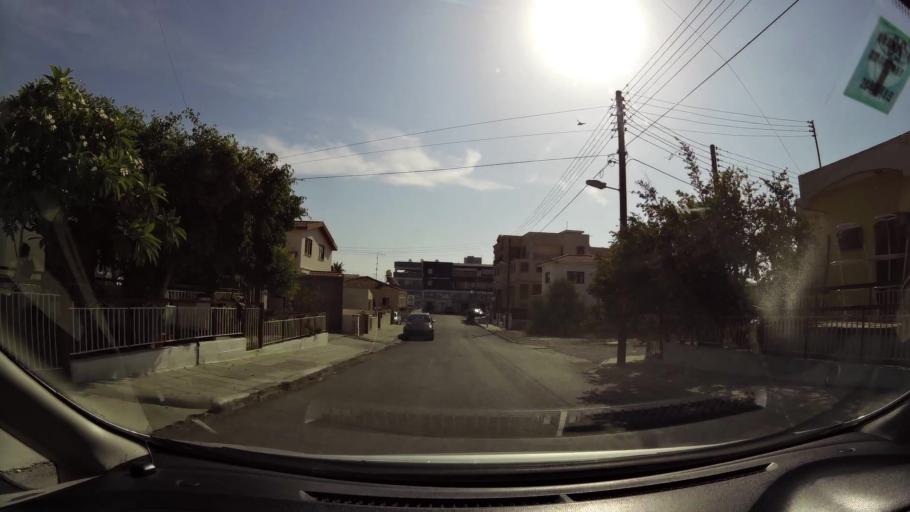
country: CY
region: Larnaka
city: Aradippou
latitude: 34.9470
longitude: 33.5905
